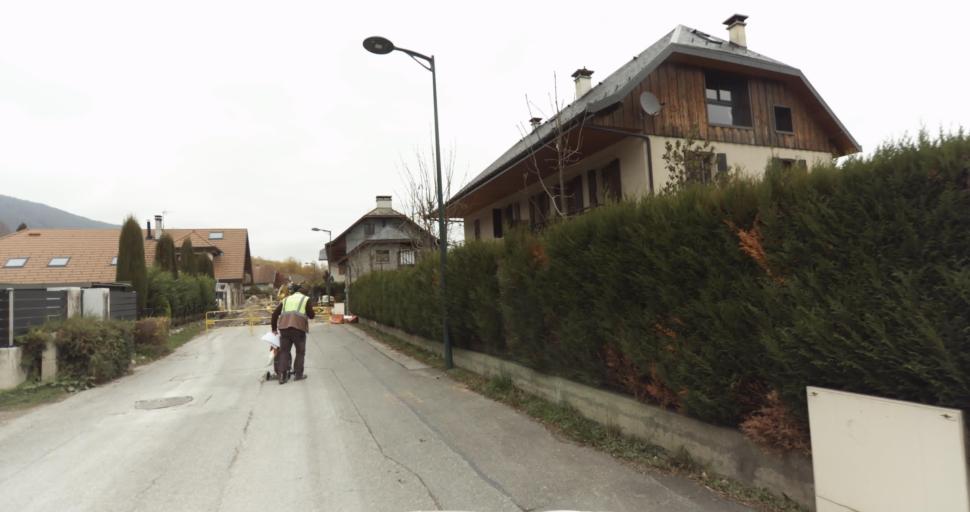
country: FR
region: Rhone-Alpes
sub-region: Departement de la Haute-Savoie
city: Saint-Jorioz
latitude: 45.8314
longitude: 6.1512
